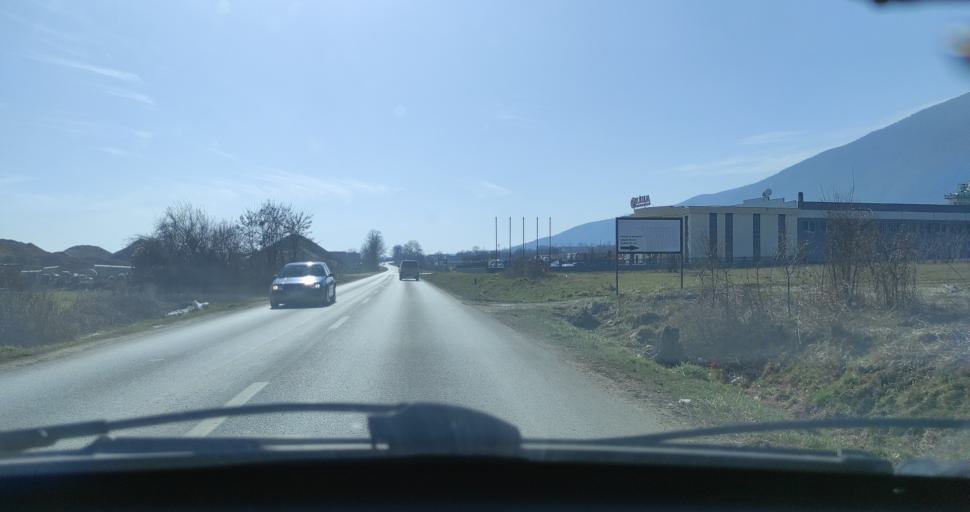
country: XK
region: Gjakova
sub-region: Komuna e Decanit
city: Strellc i Ulet
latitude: 42.6108
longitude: 20.3021
